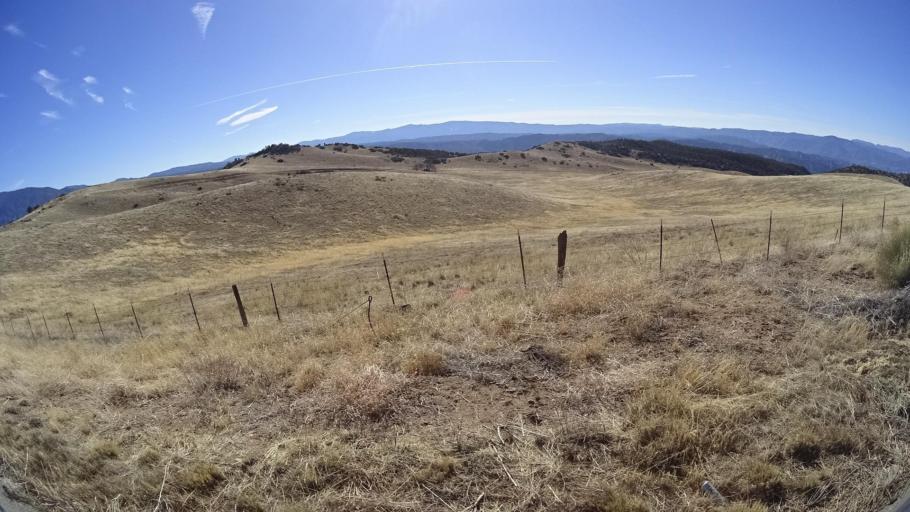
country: US
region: California
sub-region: Kern County
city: Pine Mountain Club
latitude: 34.8691
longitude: -119.3230
